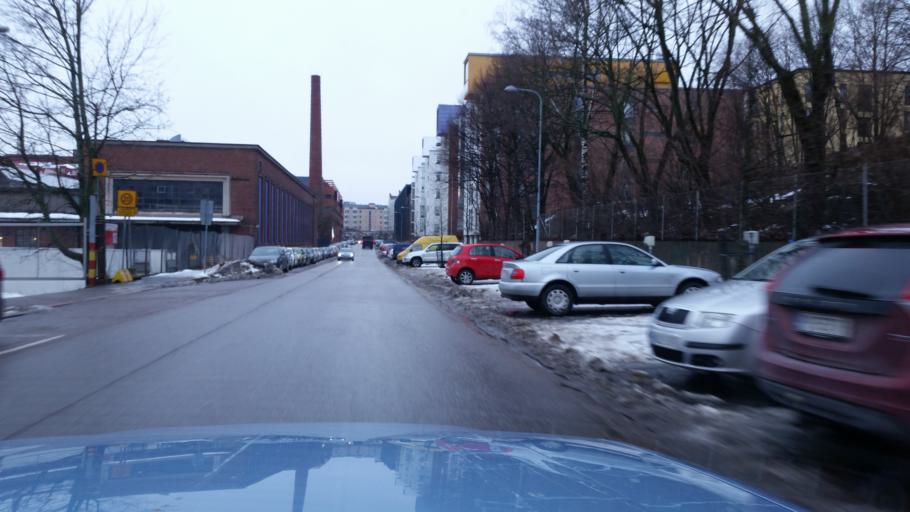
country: FI
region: Uusimaa
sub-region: Helsinki
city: Helsinki
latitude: 60.1917
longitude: 24.9711
